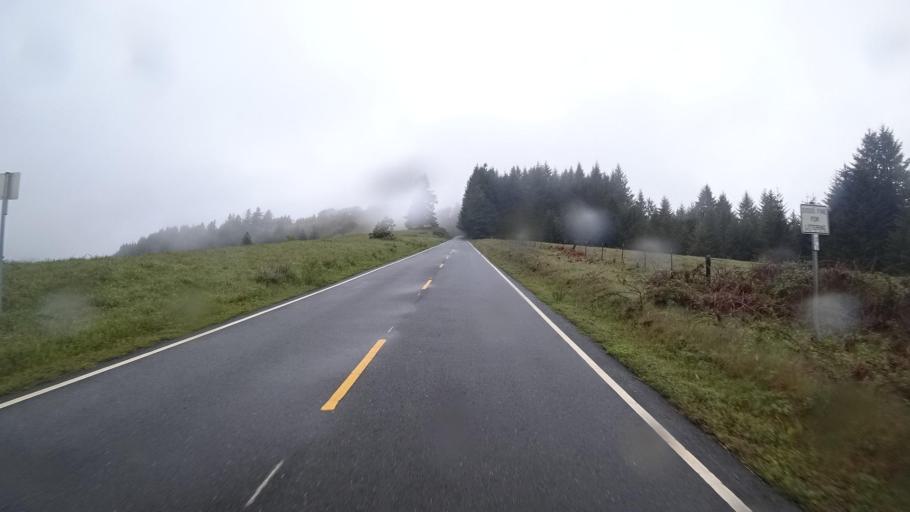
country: US
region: California
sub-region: Humboldt County
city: Westhaven-Moonstone
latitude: 41.1765
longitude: -123.9212
